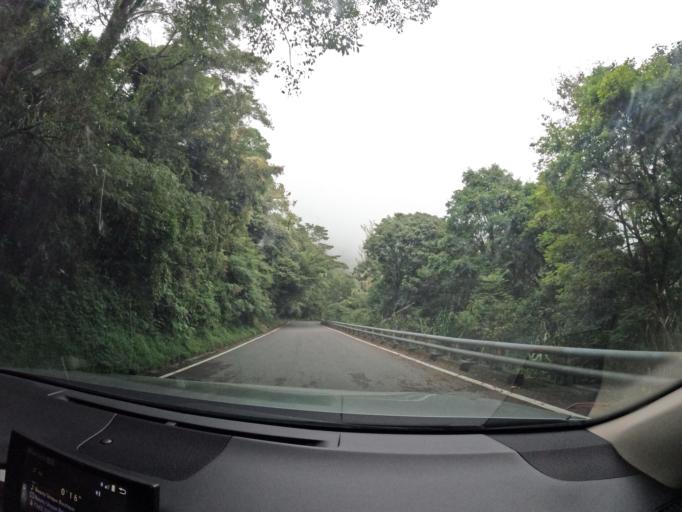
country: TW
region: Taiwan
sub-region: Taitung
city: Taitung
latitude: 23.2383
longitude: 120.9845
